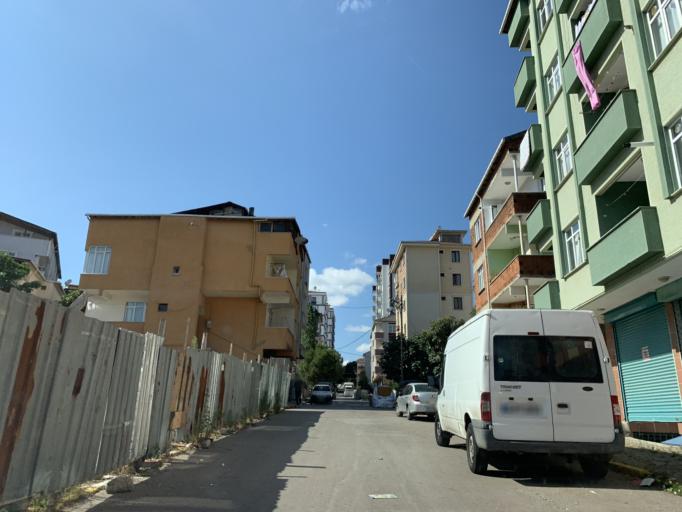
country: TR
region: Istanbul
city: Pendik
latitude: 40.8865
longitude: 29.2717
